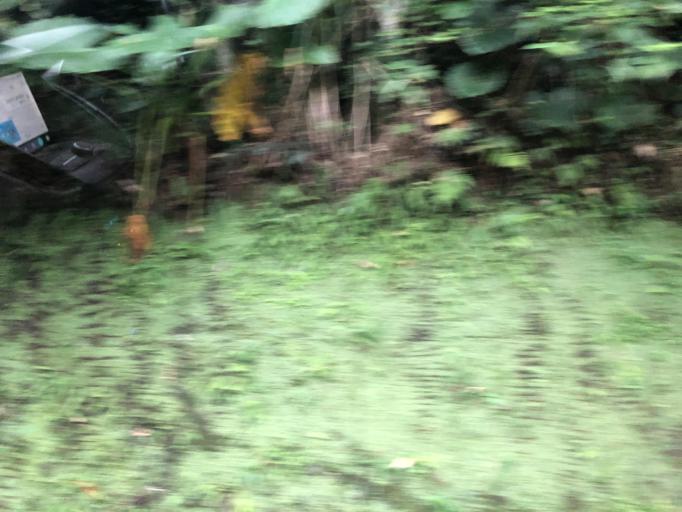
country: TW
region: Taipei
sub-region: Taipei
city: Banqiao
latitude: 24.8901
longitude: 121.4272
